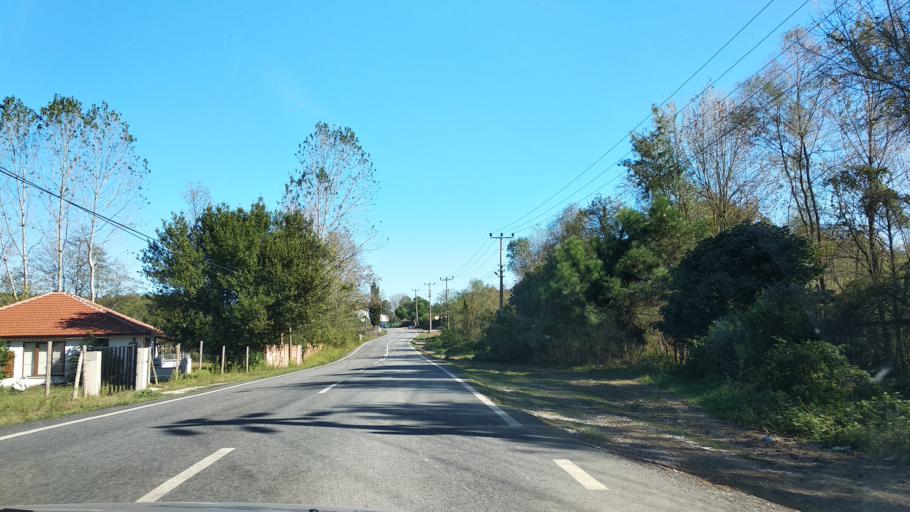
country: TR
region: Sakarya
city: Karasu
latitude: 41.1188
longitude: 30.6108
